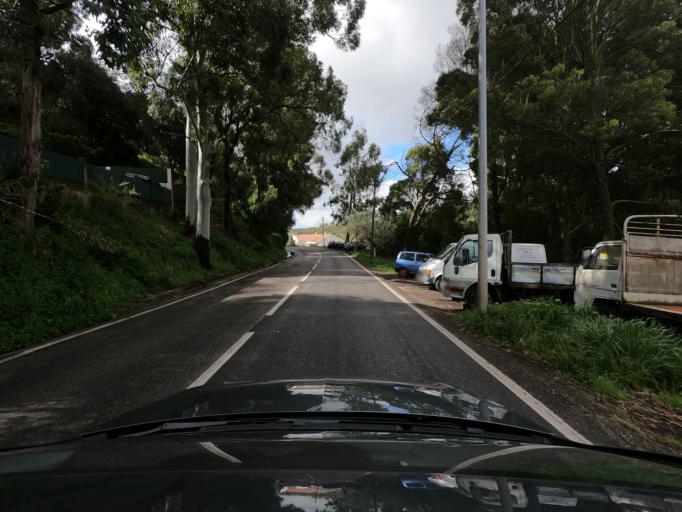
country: PT
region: Lisbon
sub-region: Oeiras
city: Quejas
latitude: 38.7343
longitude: -9.2597
